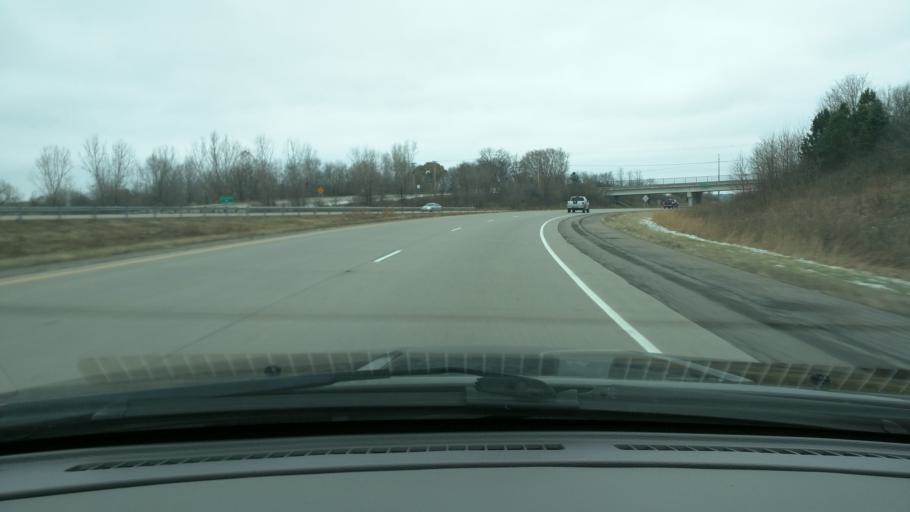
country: US
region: Minnesota
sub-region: Dakota County
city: Mendota Heights
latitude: 44.8804
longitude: -93.1636
